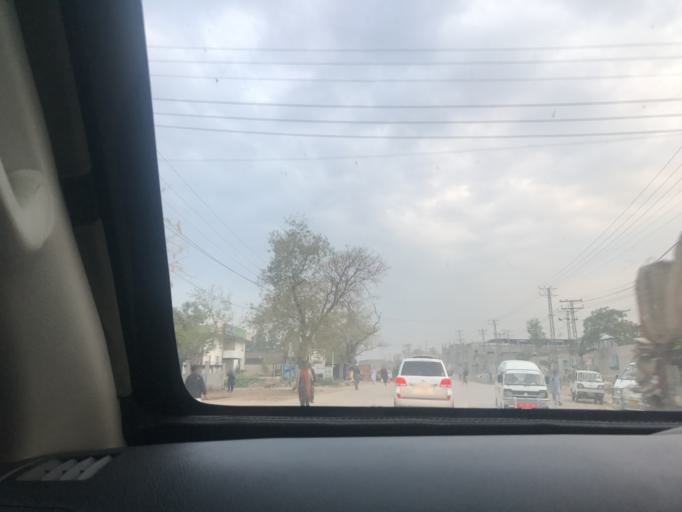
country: PK
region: Khyber Pakhtunkhwa
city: Peshawar
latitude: 33.9959
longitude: 71.4232
